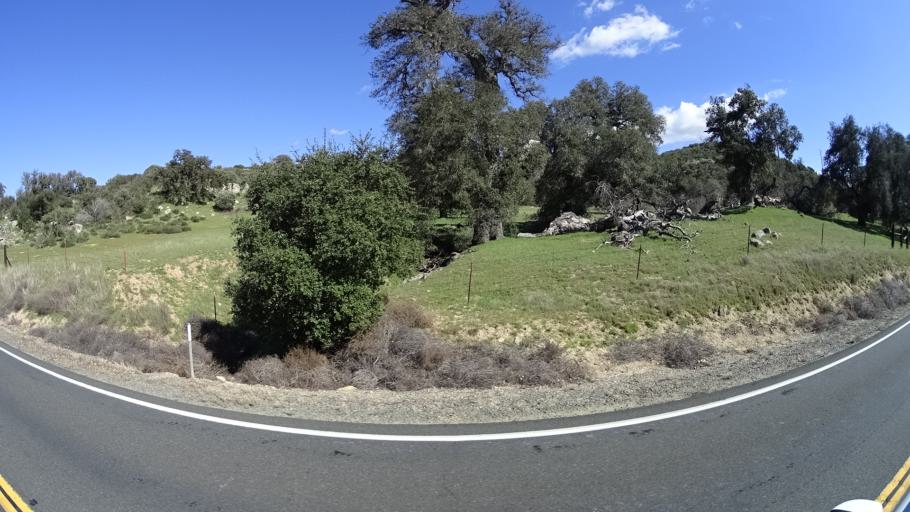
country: US
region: California
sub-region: San Diego County
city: Julian
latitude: 33.2151
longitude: -116.7096
